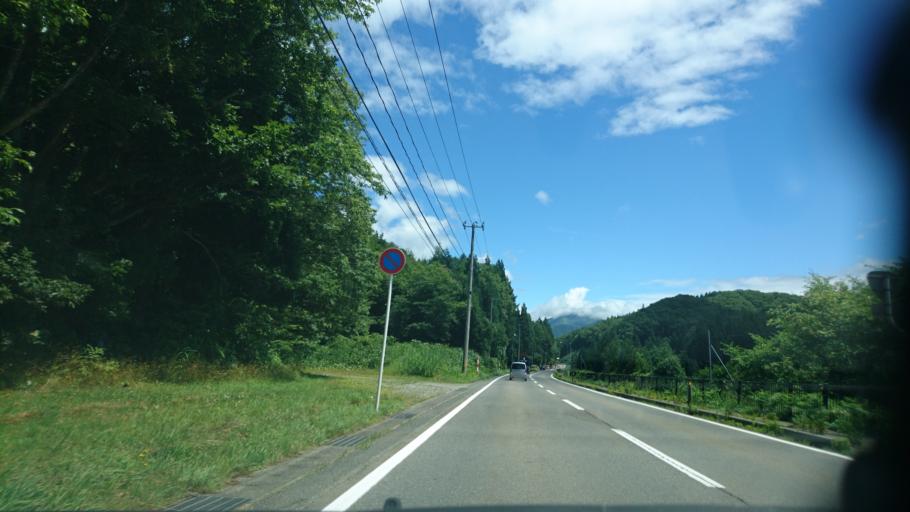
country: JP
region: Akita
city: Kakunodatemachi
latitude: 39.6709
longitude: 140.6938
